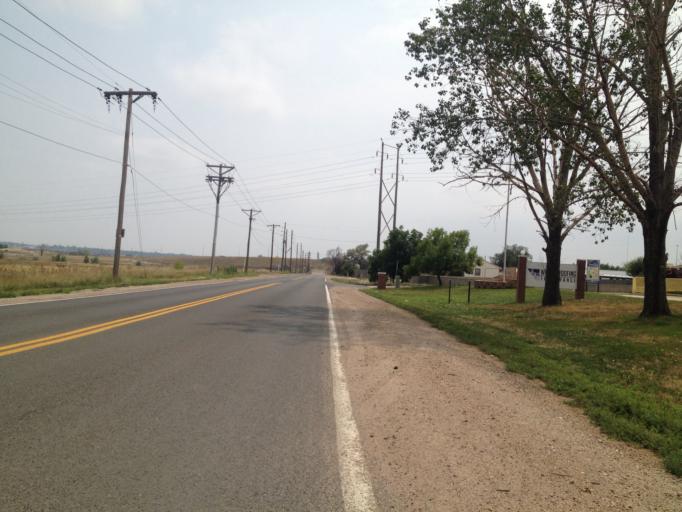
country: US
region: Colorado
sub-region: Broomfield County
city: Broomfield
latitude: 39.9069
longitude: -105.0811
